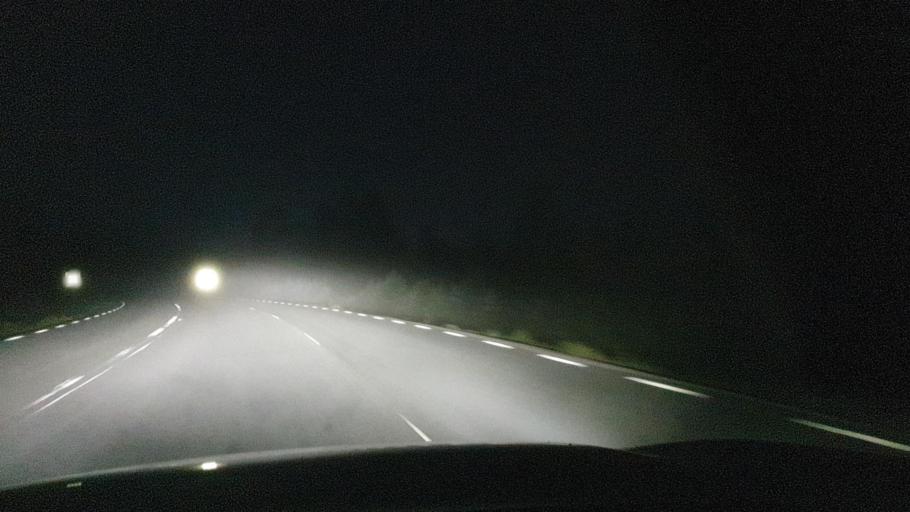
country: SE
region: Vaesternorrland
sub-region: Kramfors Kommun
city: Bollstabruk
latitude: 63.1617
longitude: 17.7879
